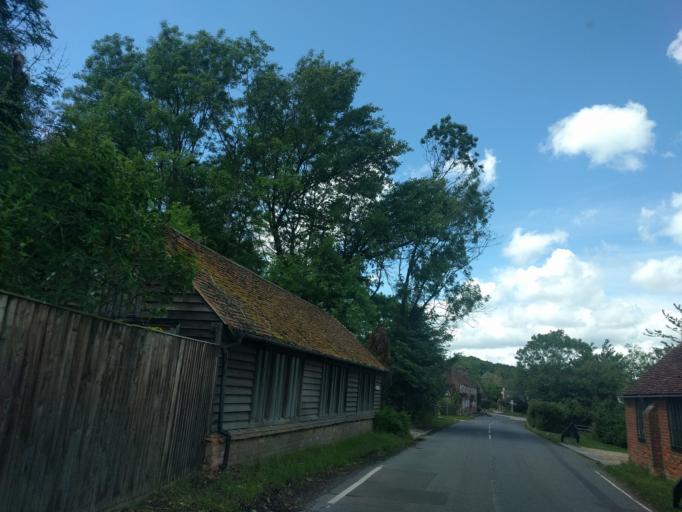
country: GB
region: England
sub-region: West Berkshire
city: Kintbury
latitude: 51.3877
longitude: -1.4086
